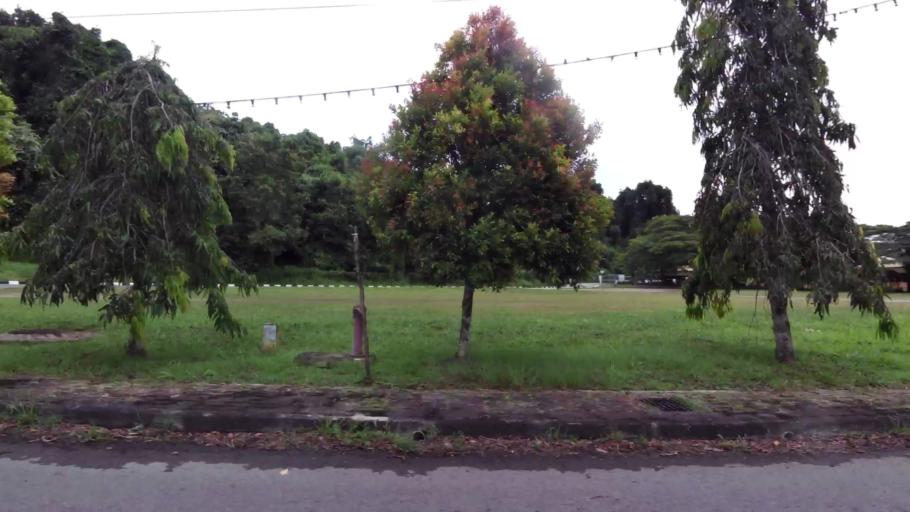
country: BN
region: Brunei and Muara
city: Bandar Seri Begawan
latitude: 4.8814
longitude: 114.9253
